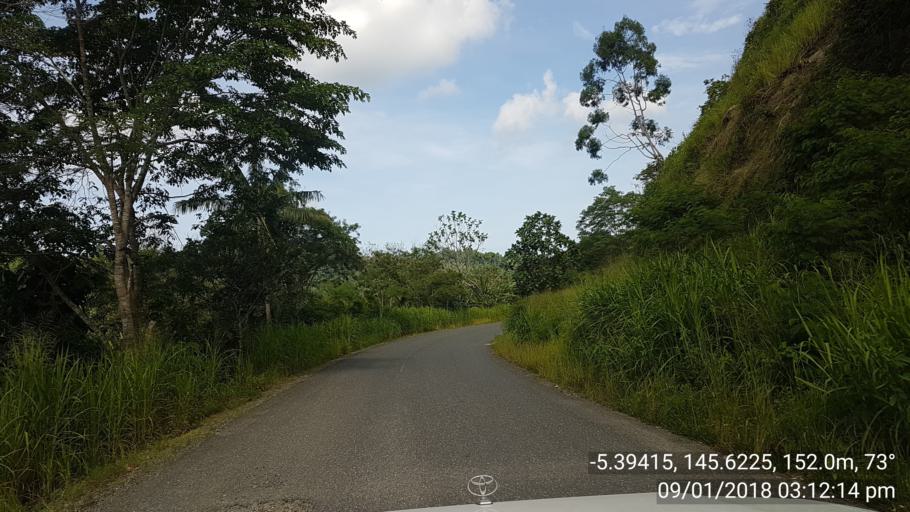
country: PG
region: Madang
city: Madang
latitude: -5.3944
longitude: 145.6220
